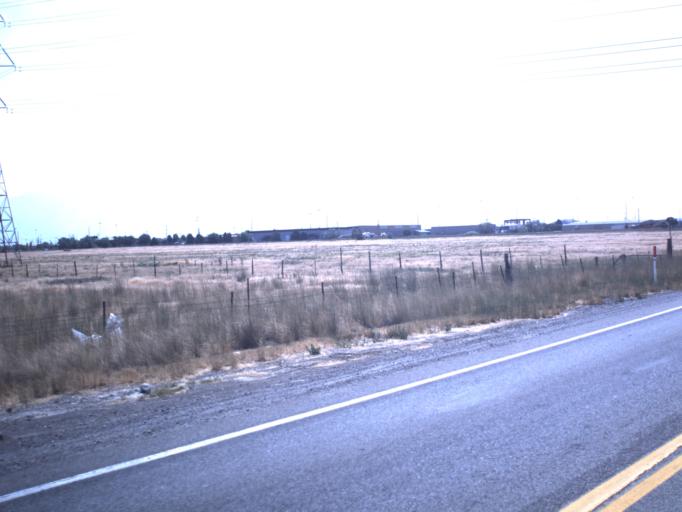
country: US
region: Utah
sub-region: Salt Lake County
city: West Valley City
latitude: 40.7587
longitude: -112.0250
